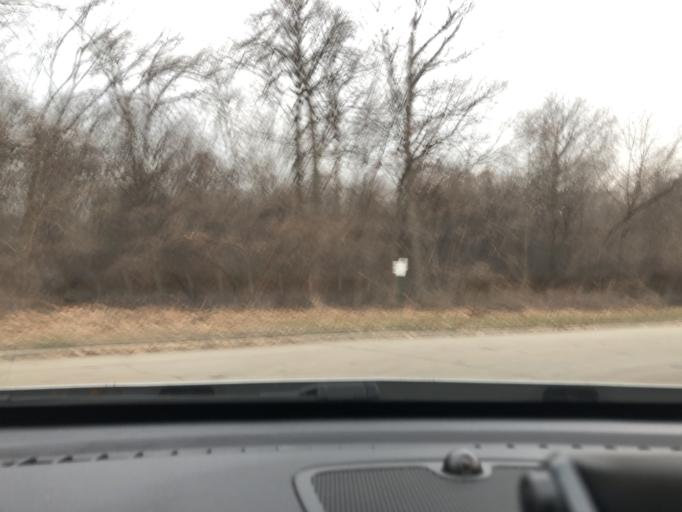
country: US
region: Michigan
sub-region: Wayne County
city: Allen Park
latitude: 42.2919
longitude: -83.2265
